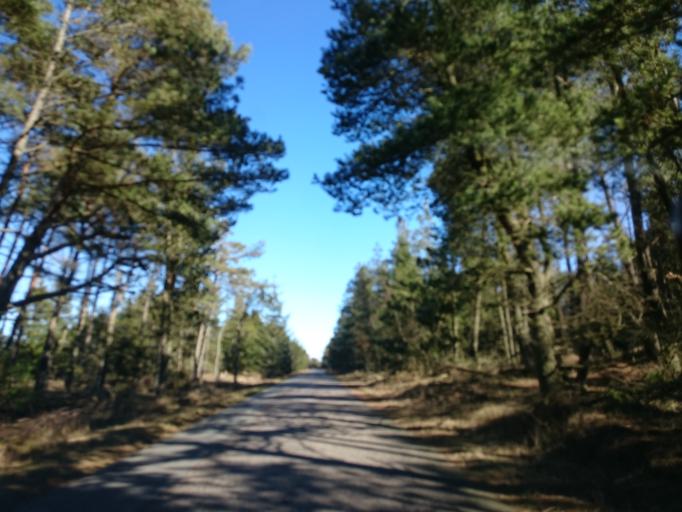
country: DK
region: North Denmark
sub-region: Hjorring Kommune
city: Sindal
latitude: 57.6245
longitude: 10.3216
